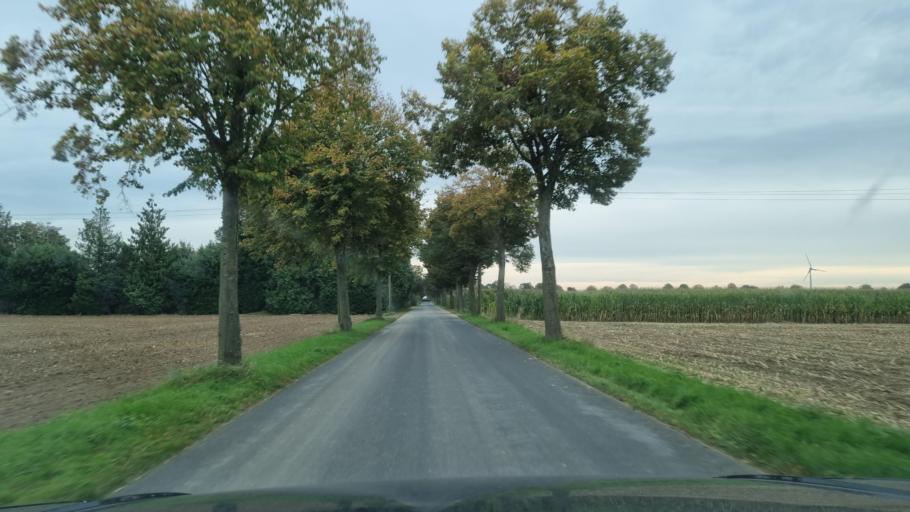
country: DE
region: North Rhine-Westphalia
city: Kalkar
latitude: 51.7179
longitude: 6.2474
